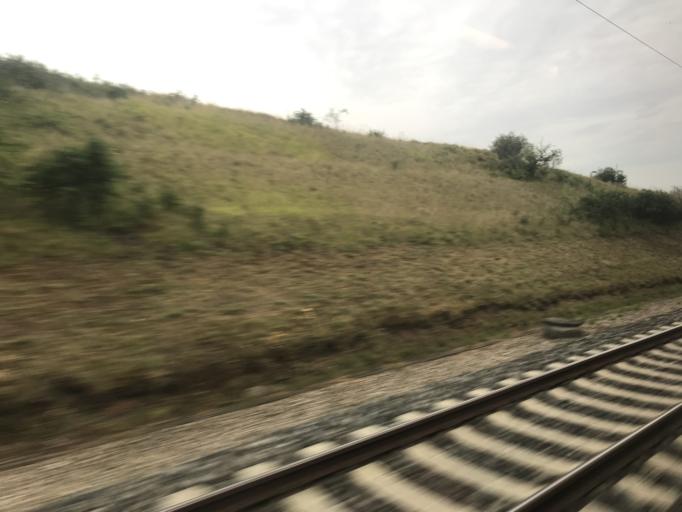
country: DE
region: Bavaria
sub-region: Regierungsbezirk Unterfranken
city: Bergtheim
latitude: 49.9138
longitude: 10.0853
